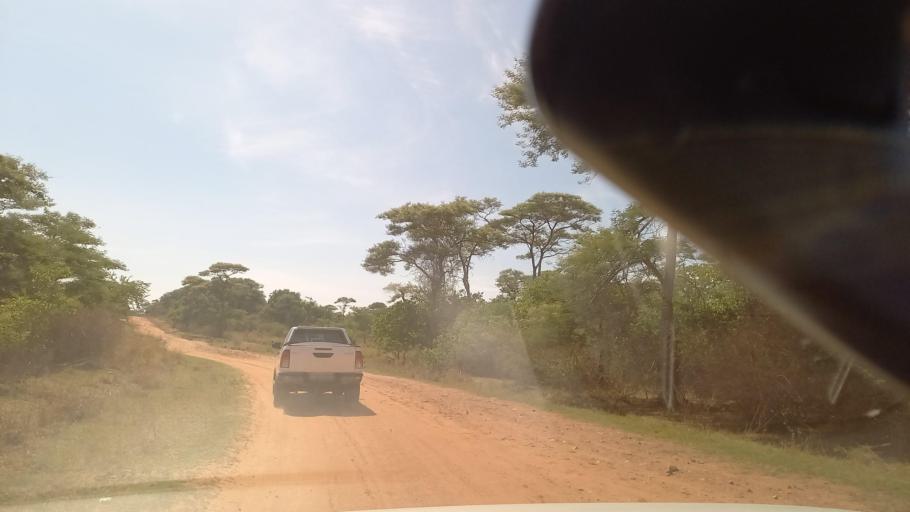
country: ZM
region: Southern
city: Mazabuka
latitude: -16.0402
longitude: 27.6191
